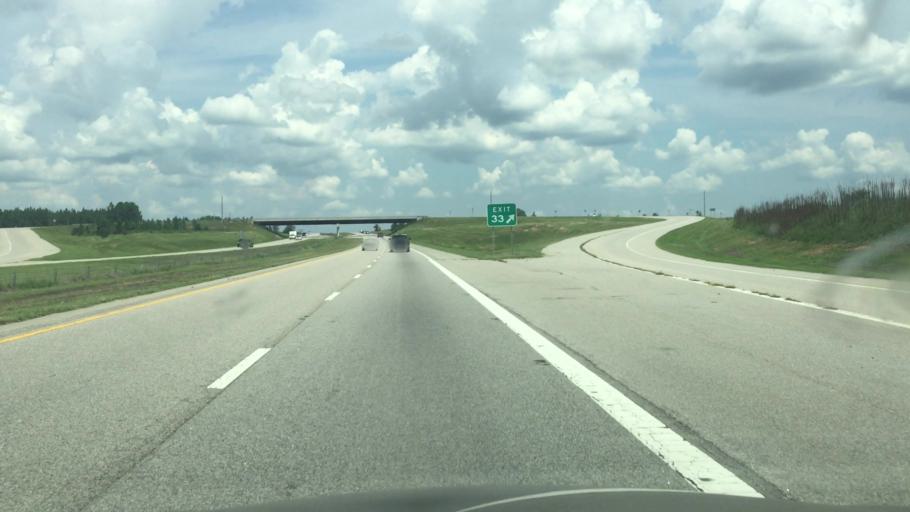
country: US
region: North Carolina
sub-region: Richmond County
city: Ellerbe
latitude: 35.1434
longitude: -79.7137
